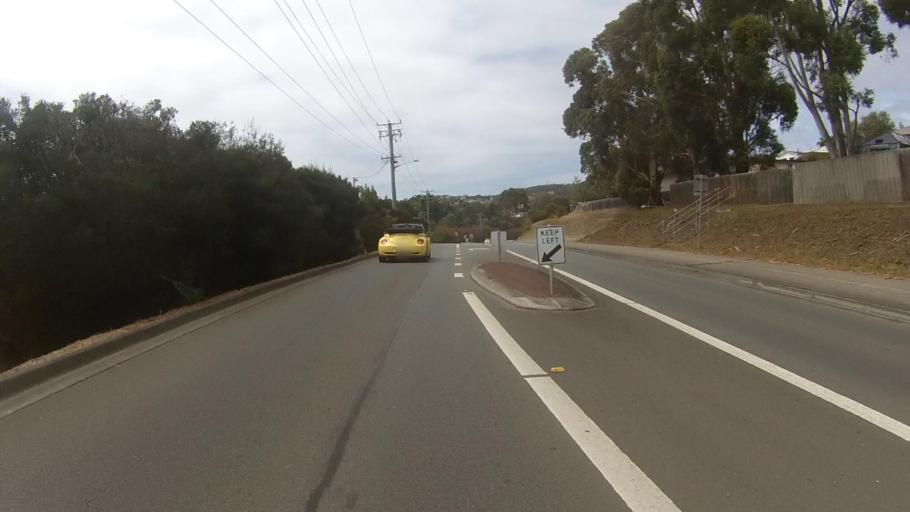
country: AU
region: Tasmania
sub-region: Kingborough
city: Kingston
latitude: -42.9723
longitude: 147.2981
